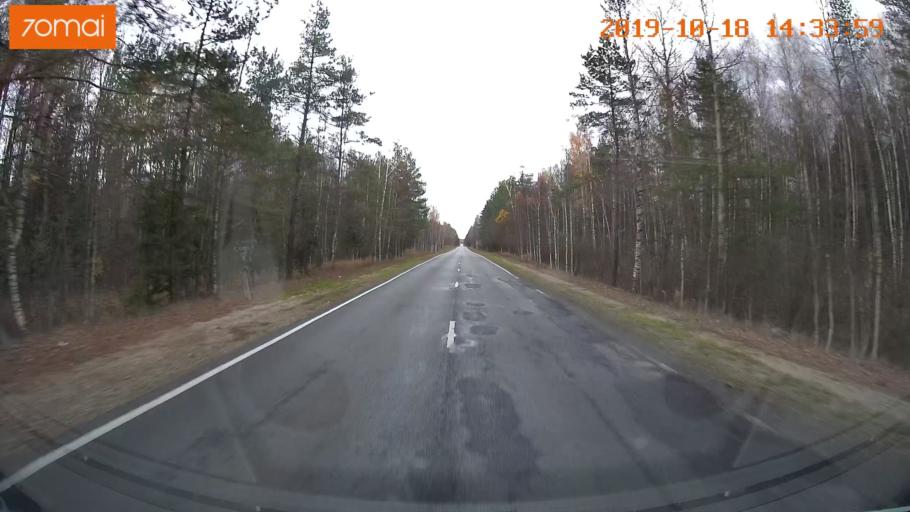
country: RU
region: Vladimir
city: Velikodvorskiy
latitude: 55.2074
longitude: 40.6075
